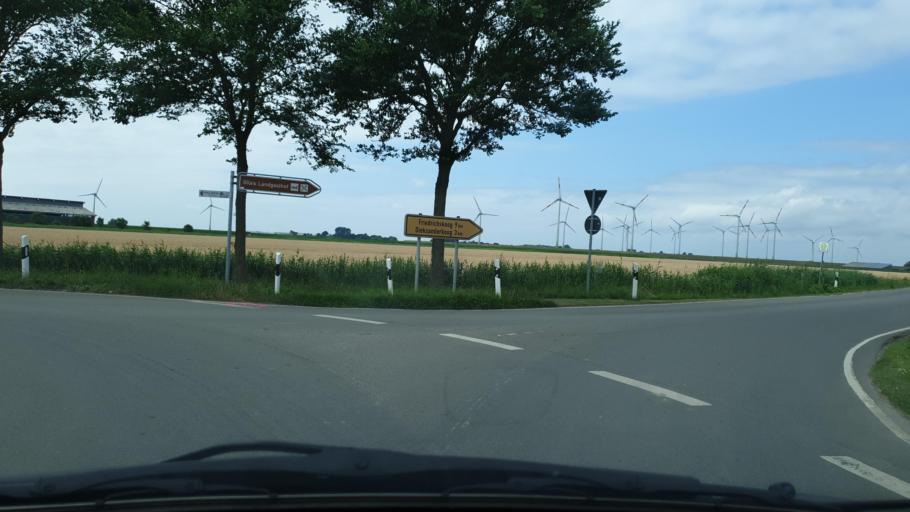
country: DE
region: Schleswig-Holstein
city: Kronprinzenkoog
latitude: 53.9469
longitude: 8.9402
